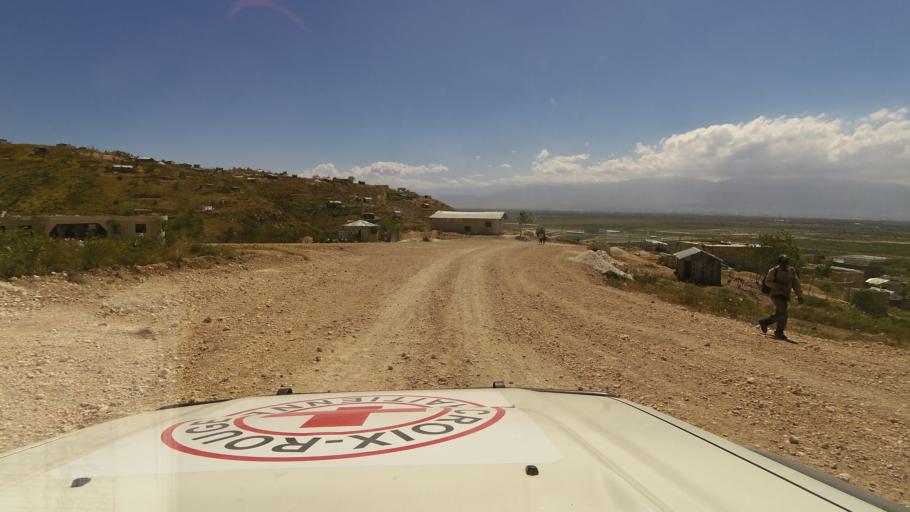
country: HT
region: Ouest
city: Croix des Bouquets
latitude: 18.6678
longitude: -72.2931
